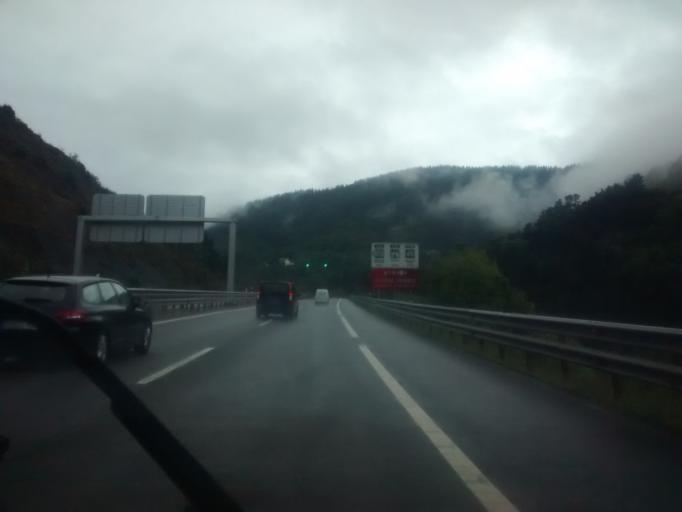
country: ES
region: Basque Country
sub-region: Provincia de Guipuzcoa
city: Elgoibar
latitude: 43.1868
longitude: -2.4288
